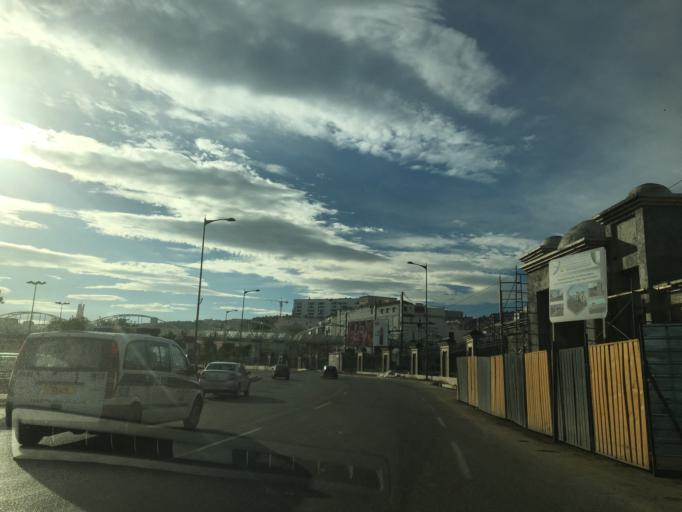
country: DZ
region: Alger
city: Algiers
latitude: 36.7656
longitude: 3.0575
